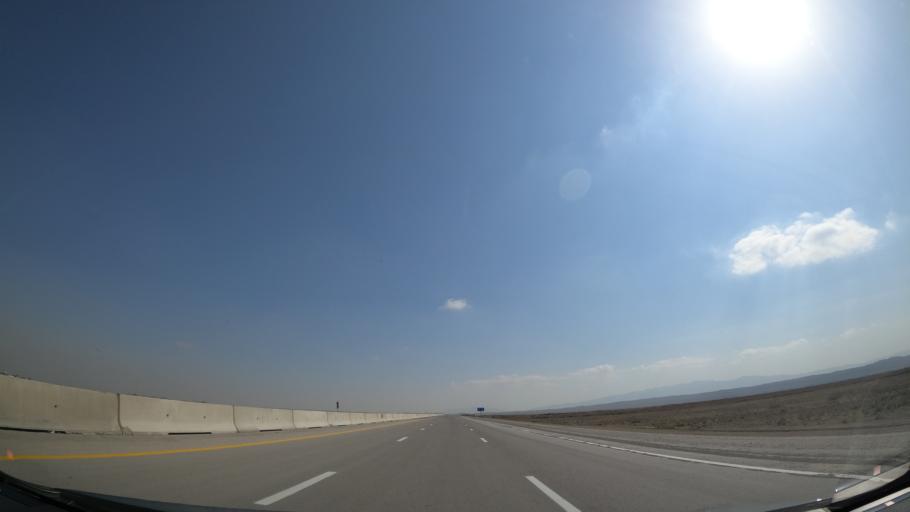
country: IR
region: Alborz
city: Nazarabad
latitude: 35.8386
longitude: 50.4896
